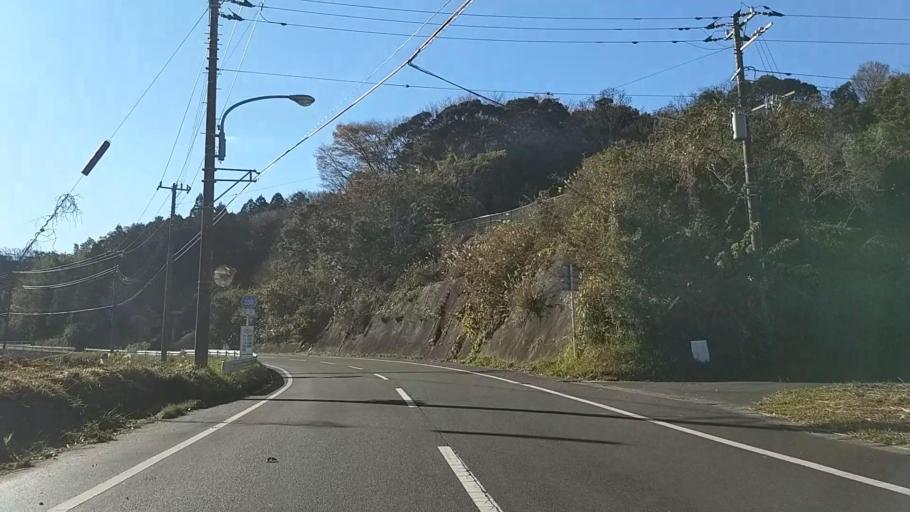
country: JP
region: Chiba
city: Futtsu
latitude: 35.2377
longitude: 139.8754
